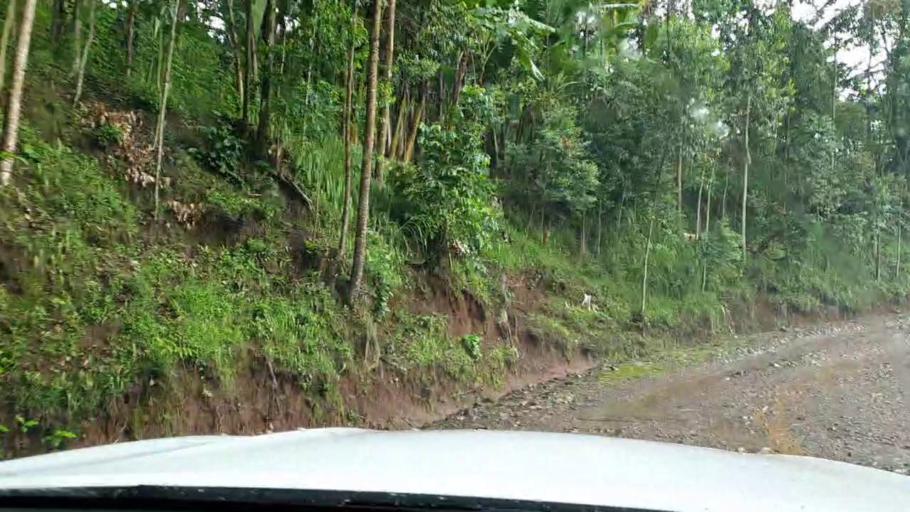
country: RW
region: Western Province
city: Cyangugu
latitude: -2.5194
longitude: 29.0445
